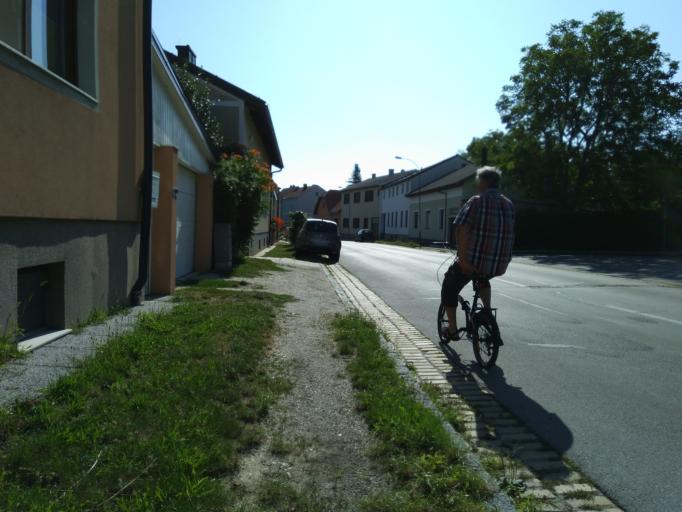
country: AT
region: Lower Austria
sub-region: Politischer Bezirk Mistelbach
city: Wolkersdorf im Weinviertel
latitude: 48.3833
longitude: 16.5050
